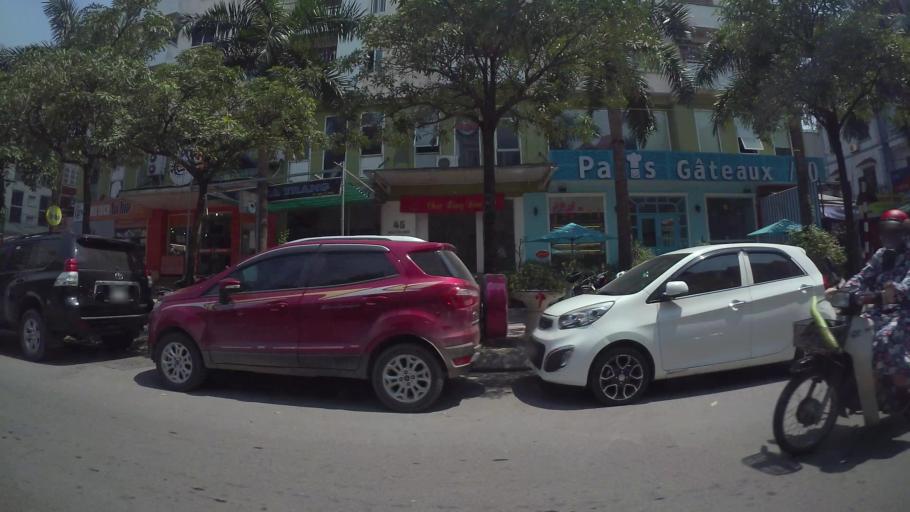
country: VN
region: Ha Noi
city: Hoan Kiem
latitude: 21.0474
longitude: 105.8771
